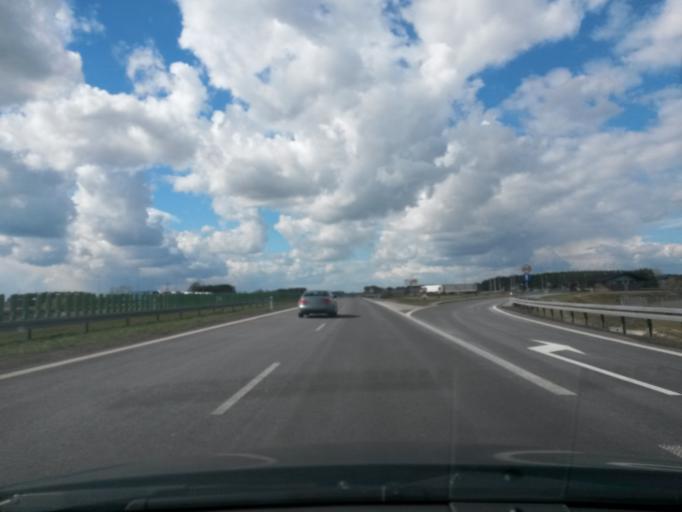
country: PL
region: Greater Poland Voivodeship
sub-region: Powiat kolski
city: Dabie
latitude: 52.0962
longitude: 18.7752
